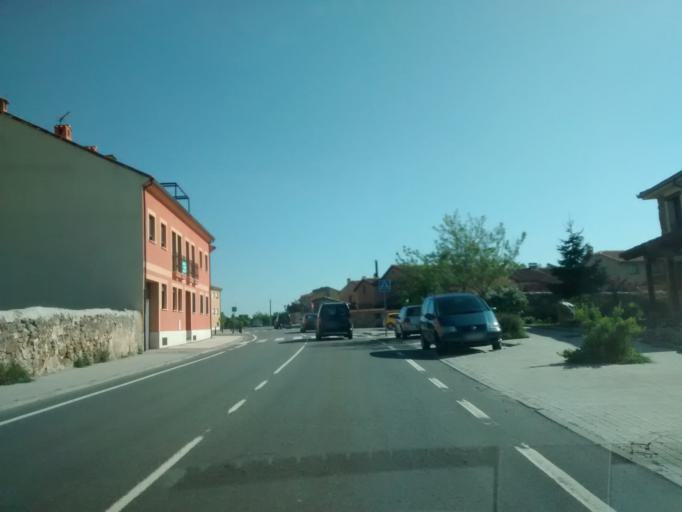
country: ES
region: Castille and Leon
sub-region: Provincia de Segovia
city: Torrecaballeros
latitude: 40.9912
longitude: -4.0232
